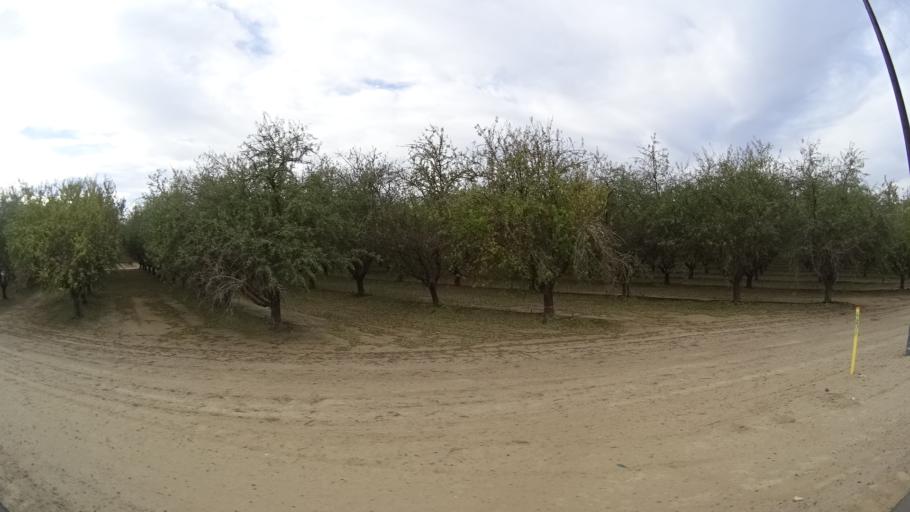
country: US
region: California
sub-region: Kern County
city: Rosedale
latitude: 35.4280
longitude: -119.1826
